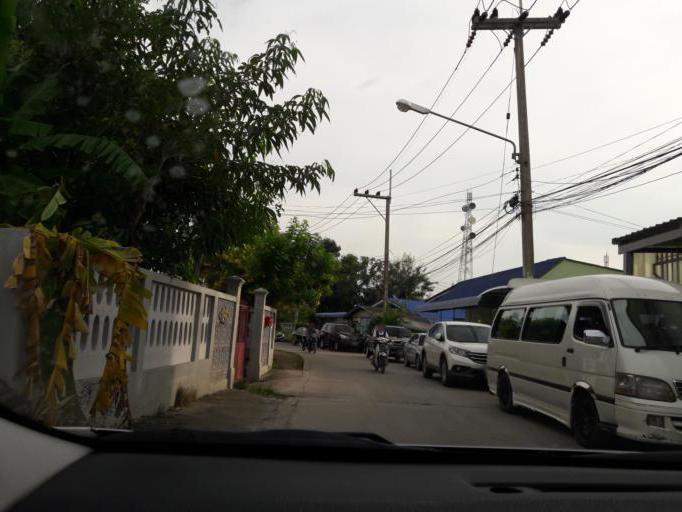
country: TH
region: Ang Thong
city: Ang Thong
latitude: 14.5891
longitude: 100.4573
